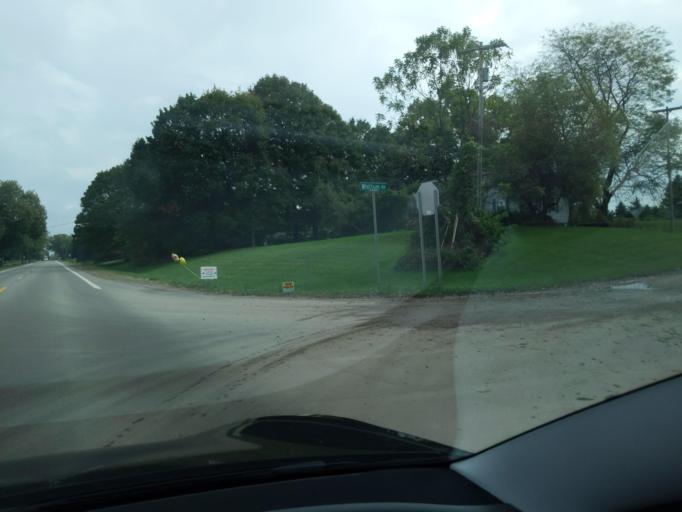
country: US
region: Michigan
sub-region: Eaton County
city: Eaton Rapids
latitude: 42.5201
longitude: -84.6802
